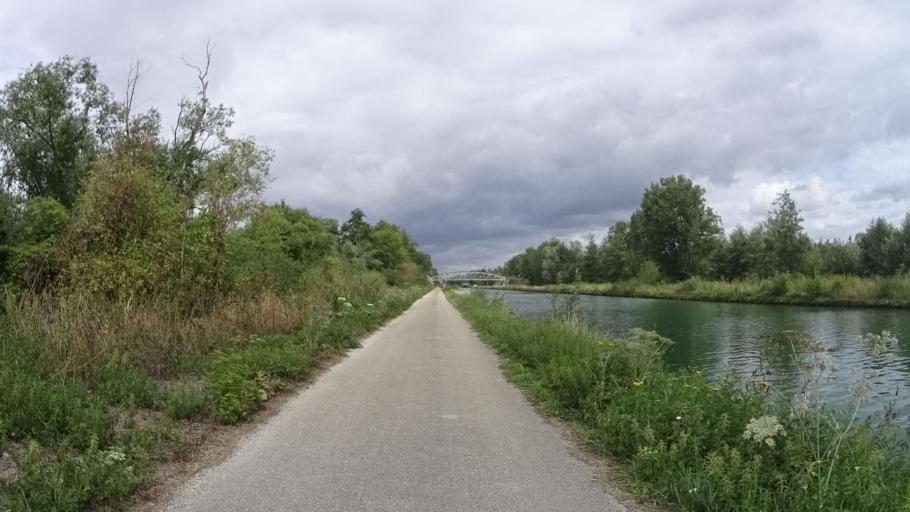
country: FR
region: Picardie
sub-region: Departement de l'Aisne
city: Viry-Noureuil
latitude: 49.6216
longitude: 3.2503
